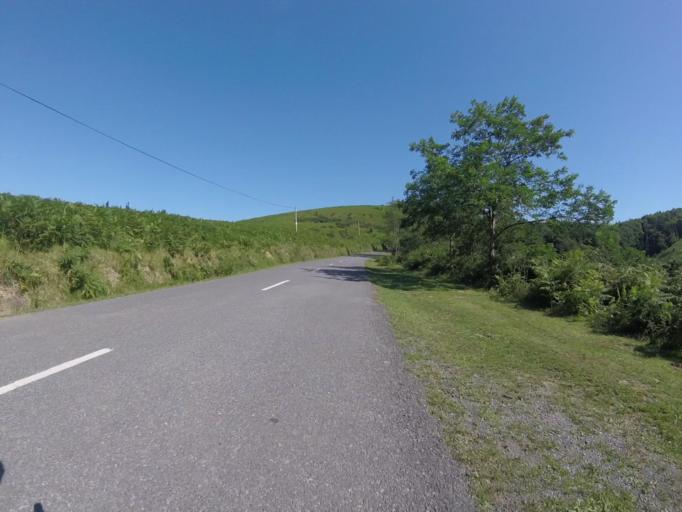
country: ES
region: Basque Country
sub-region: Provincia de Guipuzcoa
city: Irun
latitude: 43.2968
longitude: -1.8167
